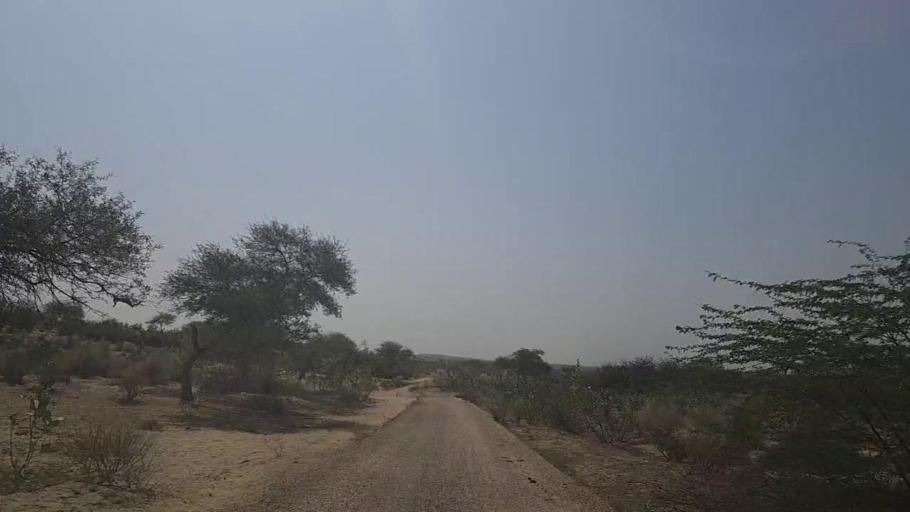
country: PK
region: Sindh
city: Naukot
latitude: 24.8147
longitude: 69.4759
